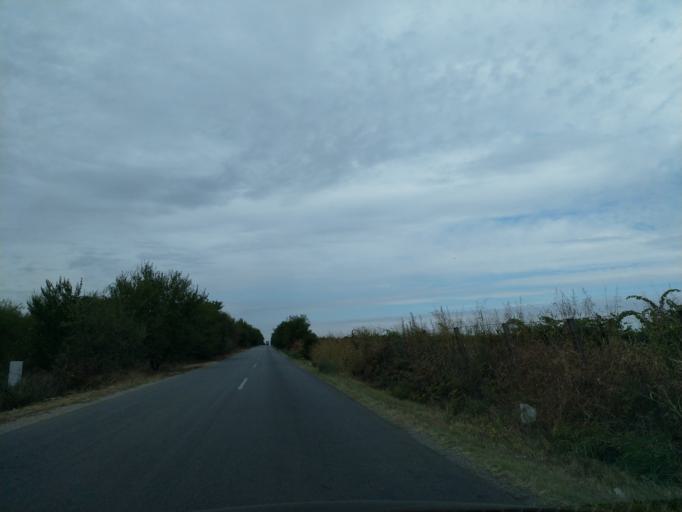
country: RS
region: Central Serbia
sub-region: Pomoravski Okrug
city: Jagodina
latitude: 43.9946
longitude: 21.2232
